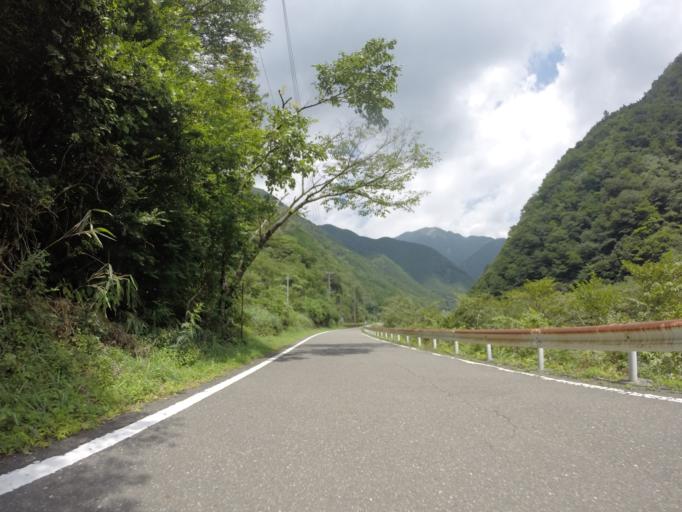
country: JP
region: Shizuoka
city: Fujinomiya
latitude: 35.2904
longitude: 138.3361
